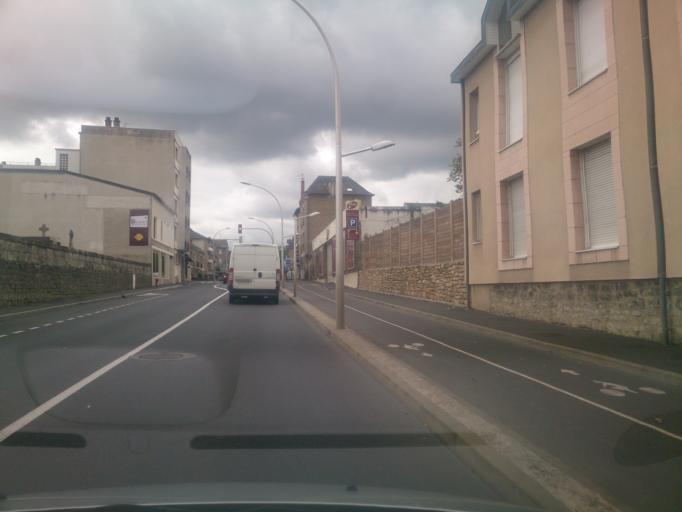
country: FR
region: Limousin
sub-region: Departement de la Correze
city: Brive-la-Gaillarde
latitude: 45.1584
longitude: 1.5405
